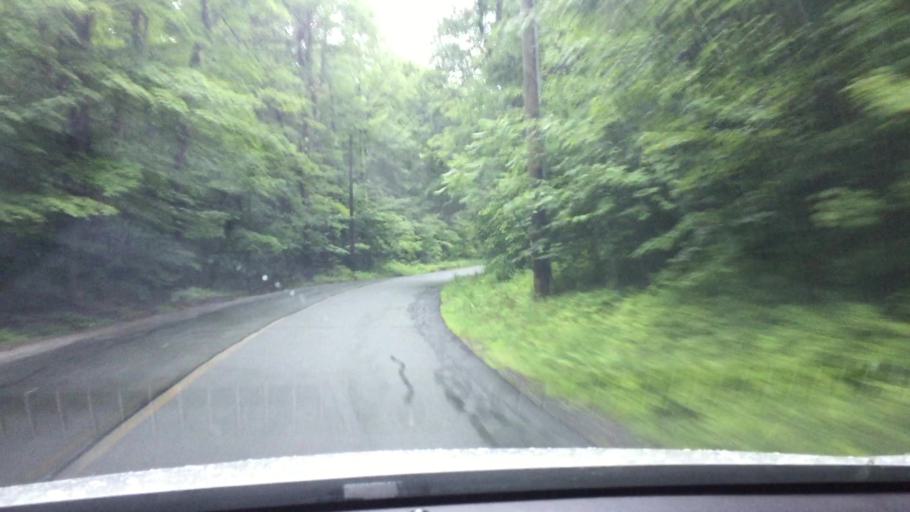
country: US
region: Massachusetts
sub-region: Berkshire County
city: Becket
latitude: 42.2818
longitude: -73.0494
